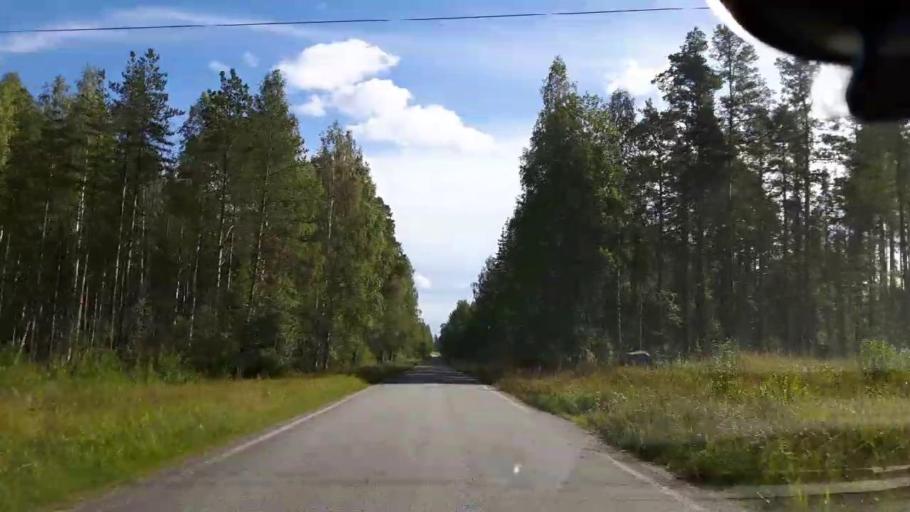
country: SE
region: Jaemtland
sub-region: Braecke Kommun
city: Braecke
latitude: 63.2191
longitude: 15.3205
